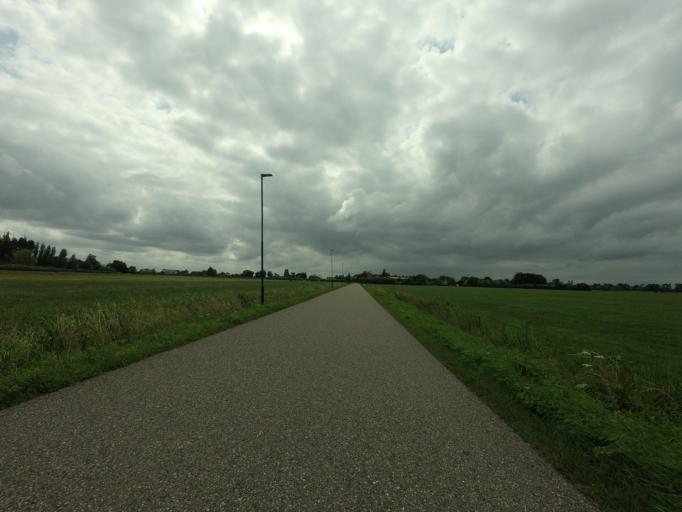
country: NL
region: South Holland
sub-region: Gemeente Giessenlanden
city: Giessenburg
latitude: 51.8642
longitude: 4.8986
